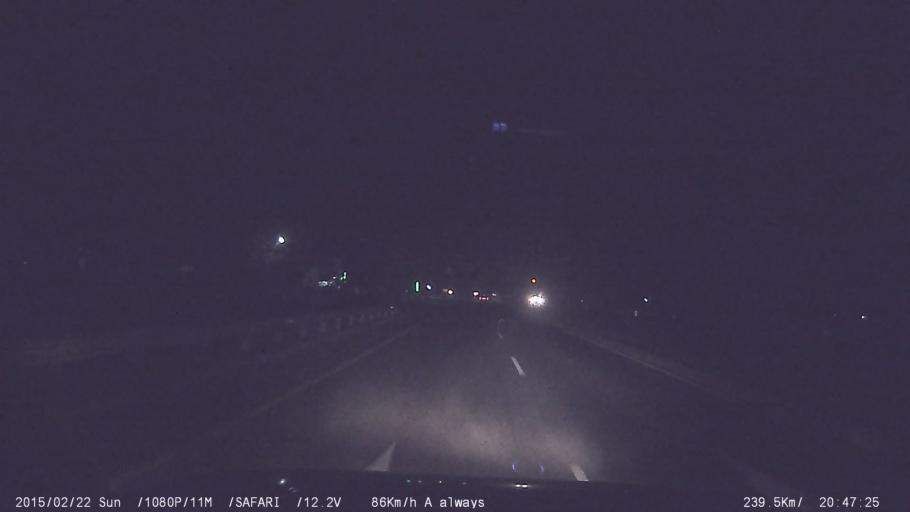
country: IN
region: Tamil Nadu
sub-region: Dindigul
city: Vedasandur
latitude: 10.4945
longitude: 77.9448
